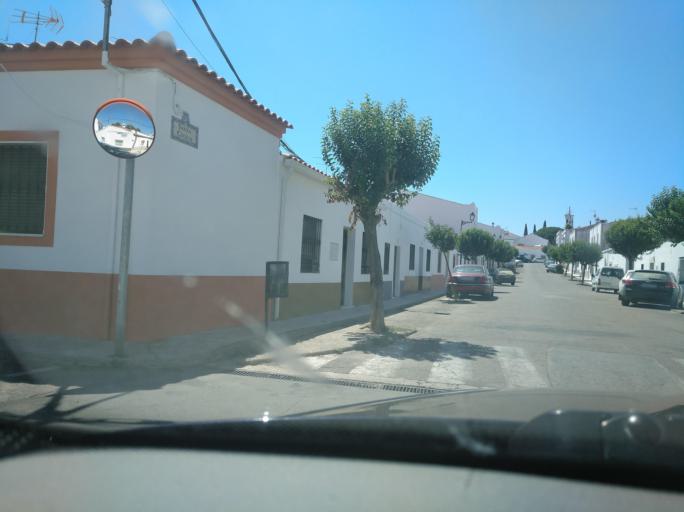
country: ES
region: Extremadura
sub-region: Provincia de Badajoz
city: Olivenza
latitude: 38.6802
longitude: -7.1015
